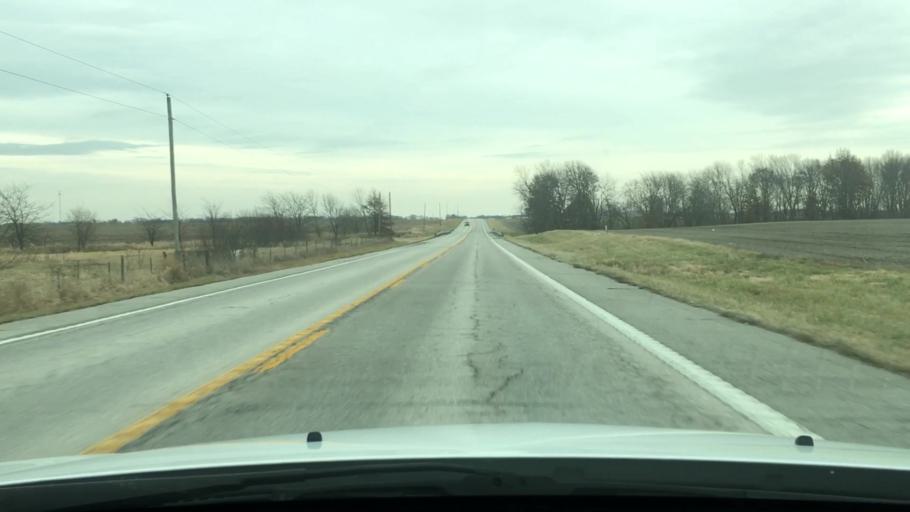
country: US
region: Missouri
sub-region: Audrain County
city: Vandalia
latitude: 39.2803
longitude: -91.6163
